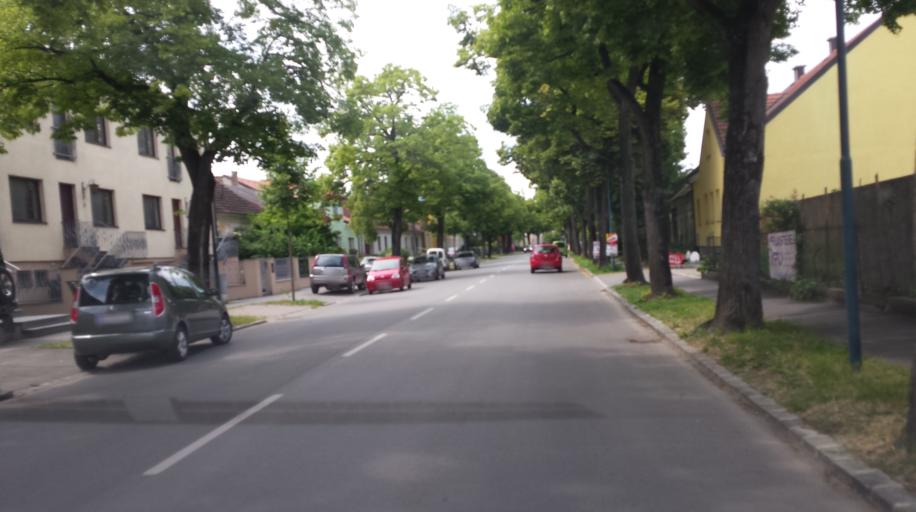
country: AT
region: Lower Austria
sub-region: Politischer Bezirk Mistelbach
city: Pillichsdorf
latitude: 48.3671
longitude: 16.5267
